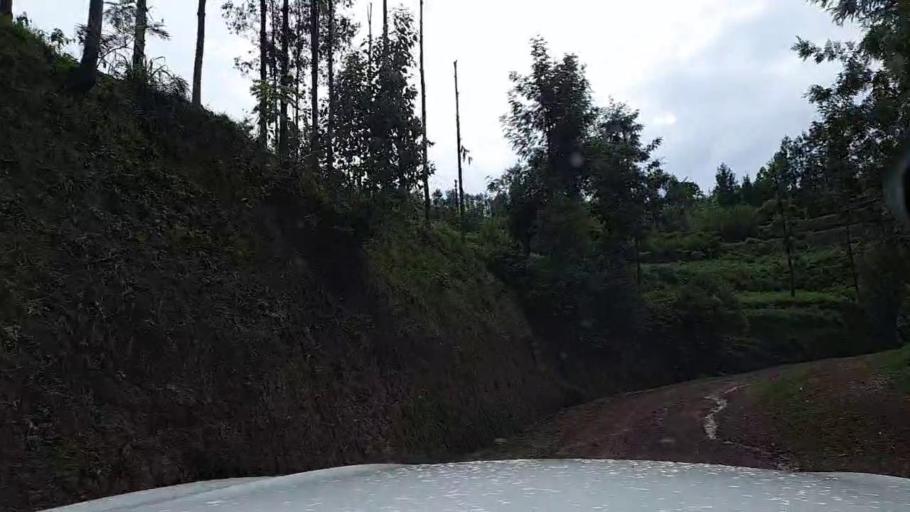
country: RW
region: Northern Province
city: Byumba
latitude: -1.7182
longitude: 29.9101
